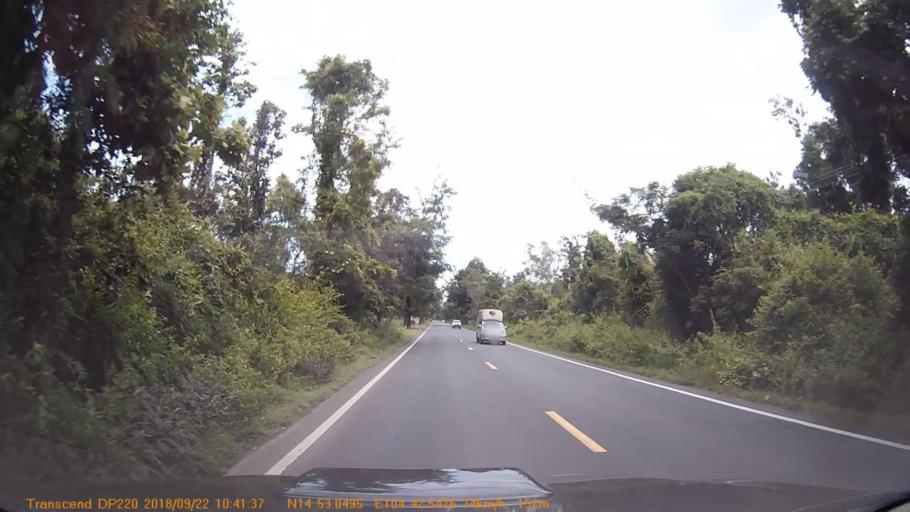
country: TH
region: Sisaket
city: Non Kho
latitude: 14.8843
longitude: 104.7092
